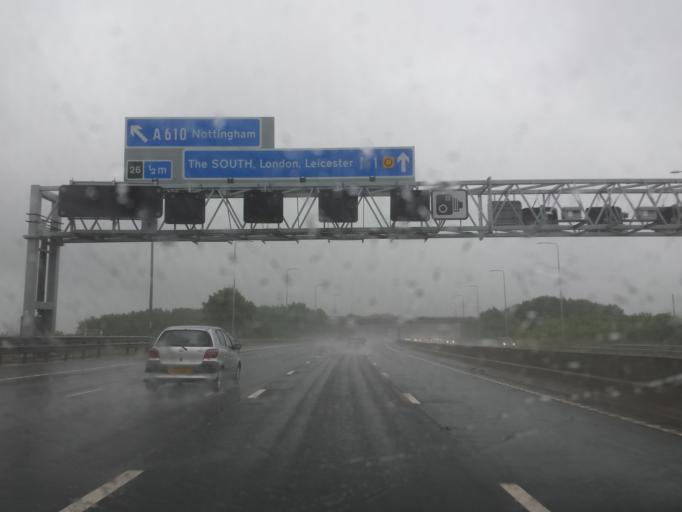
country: GB
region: England
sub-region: Nottinghamshire
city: Kimberley
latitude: 53.0077
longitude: -1.2360
